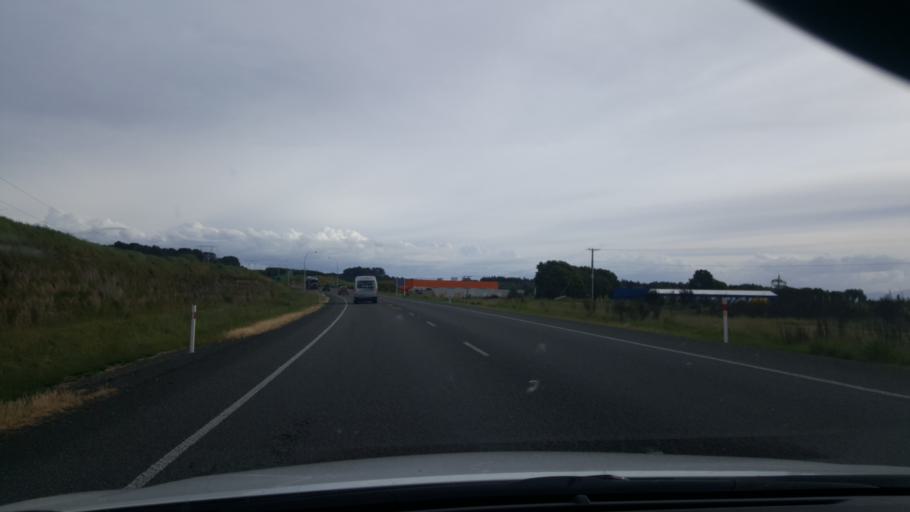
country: NZ
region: Waikato
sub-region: Taupo District
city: Taupo
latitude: -38.6993
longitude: 176.1121
